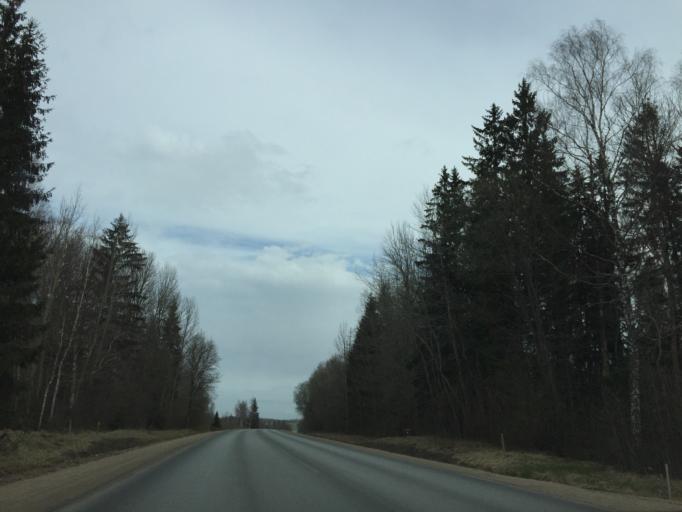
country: LV
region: Amatas Novads
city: Drabesi
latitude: 57.2400
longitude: 25.2545
